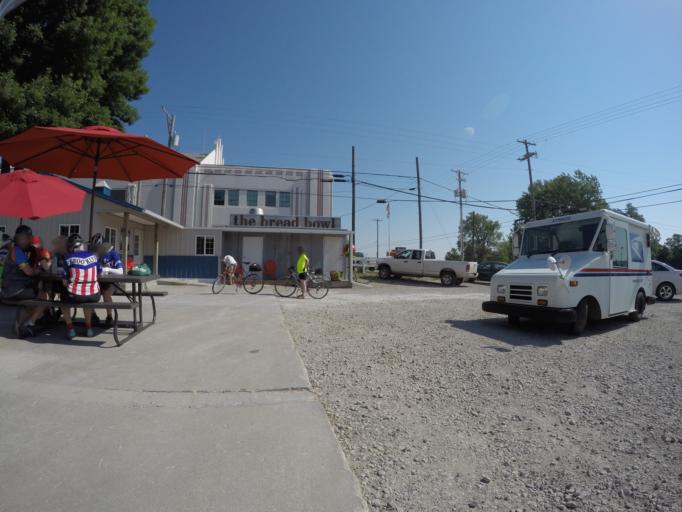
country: US
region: Kansas
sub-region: Brown County
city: Hiawatha
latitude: 39.8532
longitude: -95.5275
